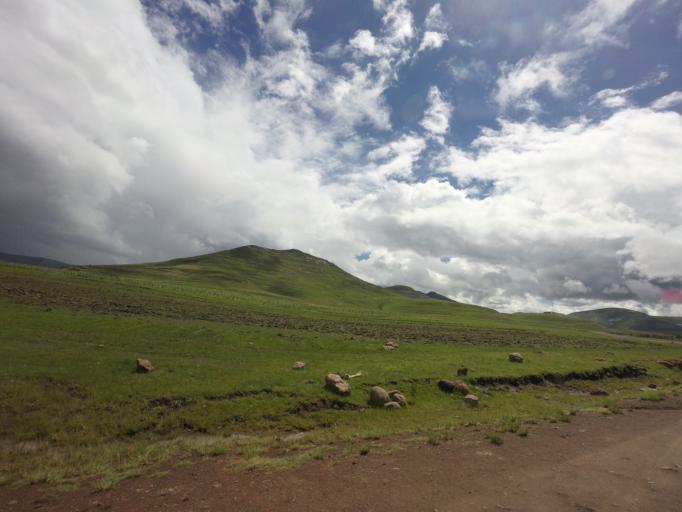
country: LS
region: Maseru
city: Nako
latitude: -29.8790
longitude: 28.0488
